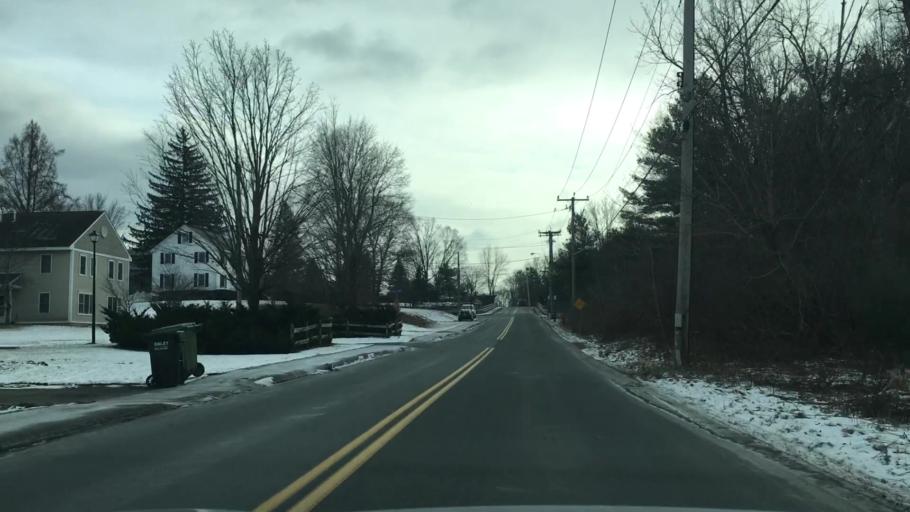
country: US
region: Massachusetts
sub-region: Berkshire County
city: Lee
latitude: 42.2985
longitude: -73.2493
